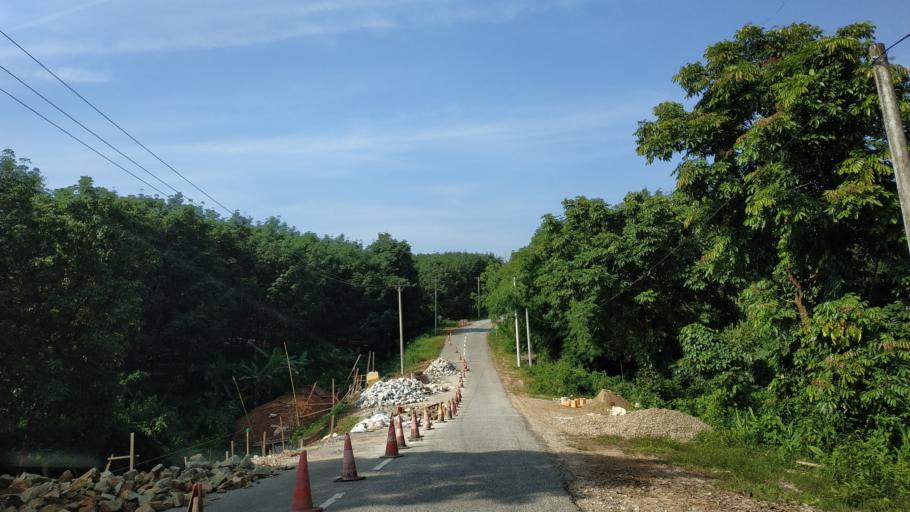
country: MM
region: Tanintharyi
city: Dawei
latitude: 14.6035
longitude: 98.1019
